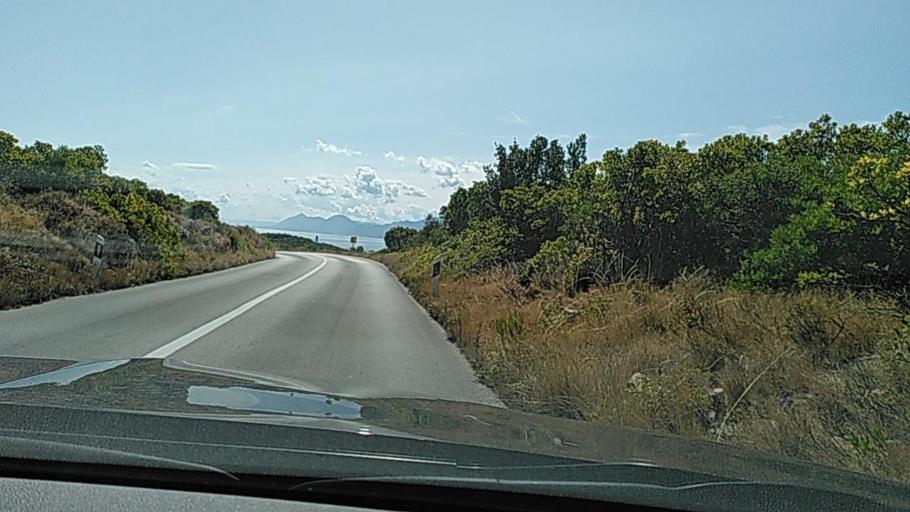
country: HR
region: Splitsko-Dalmatinska
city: Tucepi
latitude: 43.1267
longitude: 17.0910
